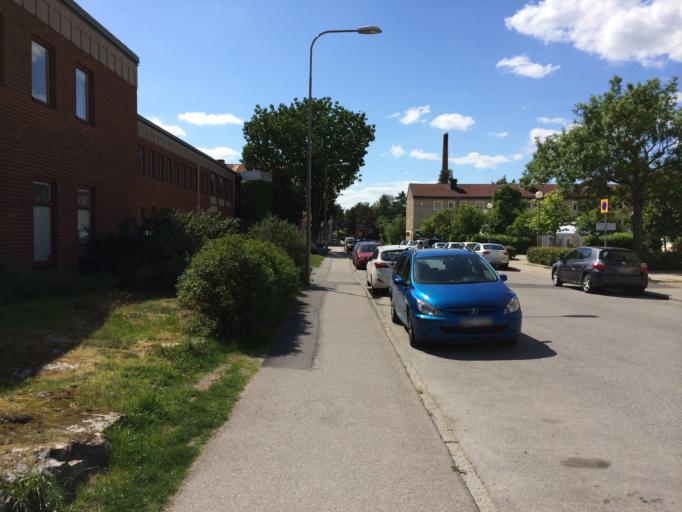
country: SE
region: Stockholm
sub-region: Huddinge Kommun
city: Segeltorp
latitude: 59.2973
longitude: 17.9847
